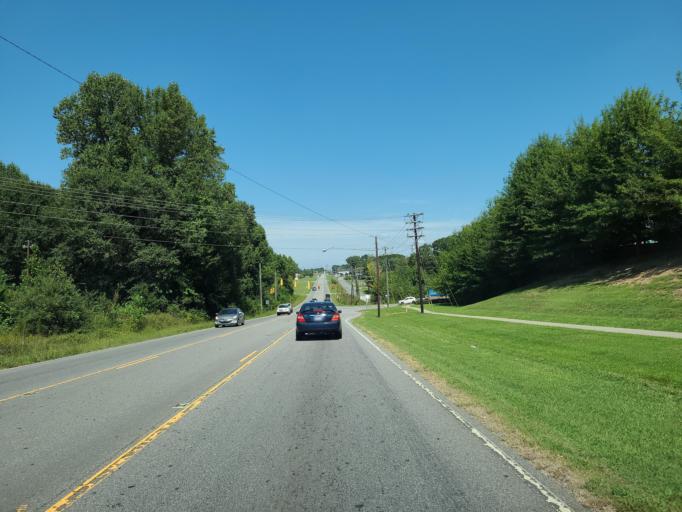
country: US
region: North Carolina
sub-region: Lincoln County
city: Lincolnton
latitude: 35.4836
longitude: -81.2427
